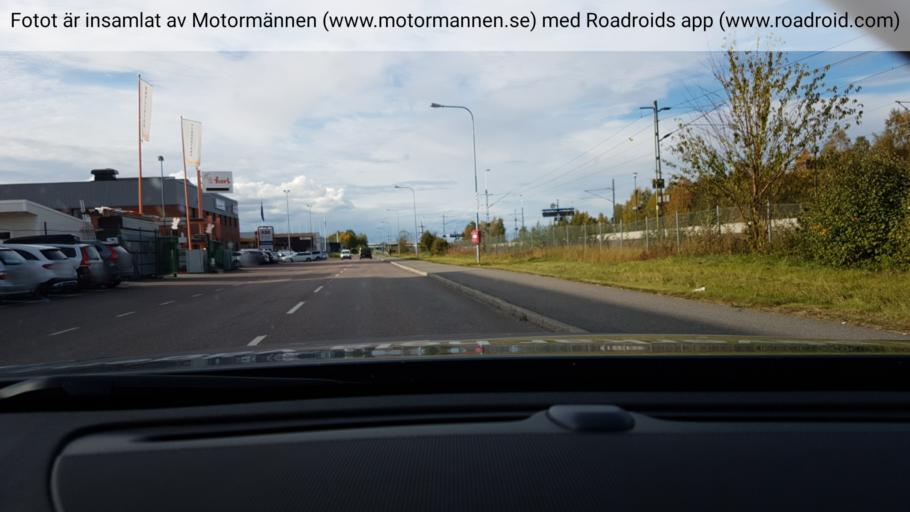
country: SE
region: Norrbotten
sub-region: Lulea Kommun
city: Bergnaset
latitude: 65.6101
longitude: 22.1204
